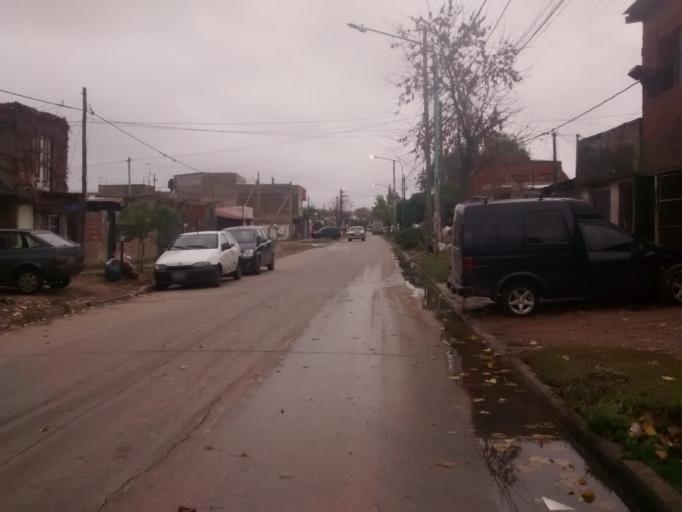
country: AR
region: Buenos Aires
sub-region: Partido de La Plata
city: La Plata
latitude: -34.8896
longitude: -57.9445
